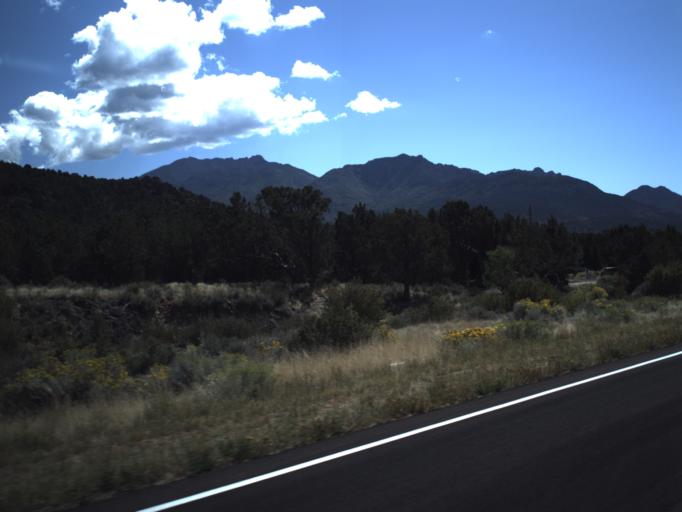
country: US
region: Utah
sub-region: Washington County
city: Enterprise
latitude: 37.4312
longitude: -113.6292
